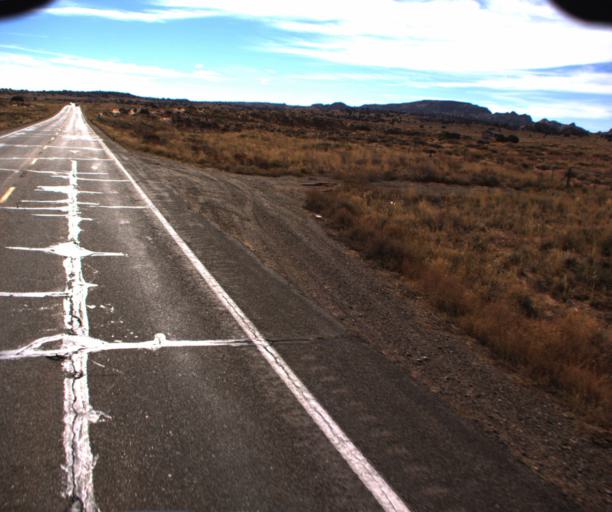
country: US
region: Arizona
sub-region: Coconino County
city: Kaibito
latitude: 36.5886
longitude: -111.1544
